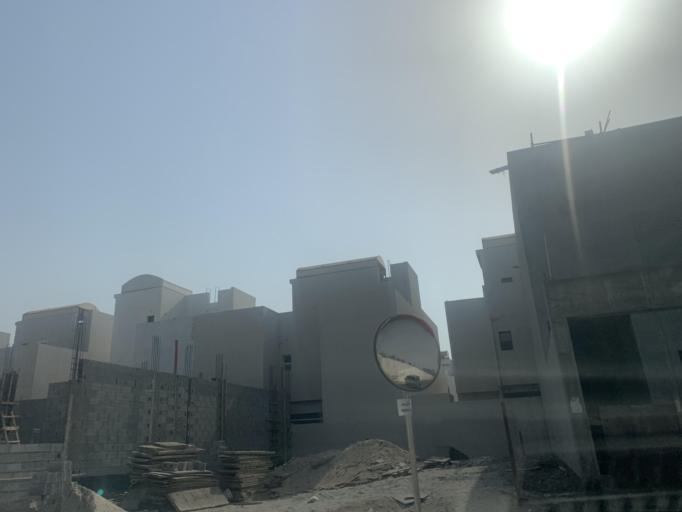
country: BH
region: Manama
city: Jidd Hafs
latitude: 26.2127
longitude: 50.4708
